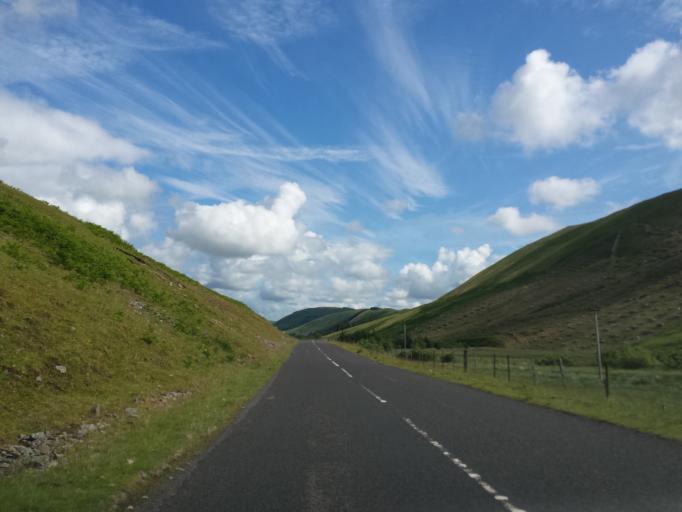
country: GB
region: Scotland
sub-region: The Scottish Borders
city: Peebles
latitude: 55.4455
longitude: -3.2248
